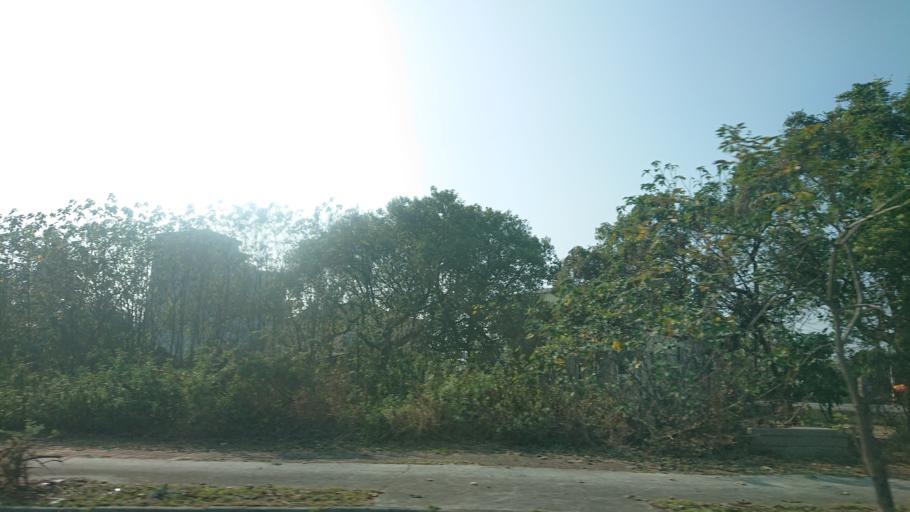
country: TW
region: Taiwan
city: Xinying
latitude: 23.3392
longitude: 120.2506
